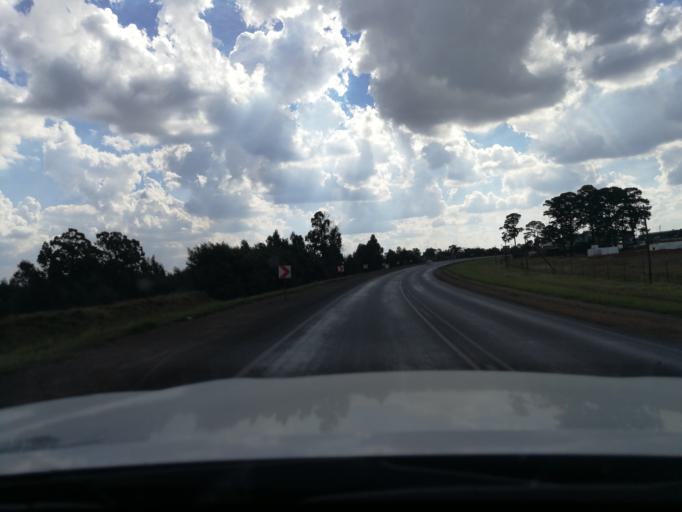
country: ZA
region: Mpumalanga
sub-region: Nkangala District Municipality
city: Middelburg
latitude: -25.8591
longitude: 29.4634
